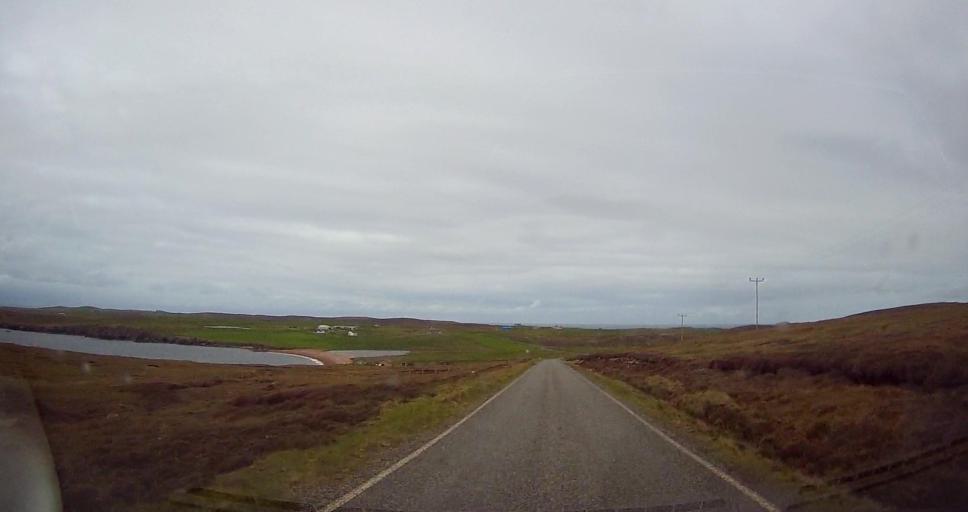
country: GB
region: Scotland
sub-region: Shetland Islands
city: Lerwick
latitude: 60.4879
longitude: -1.5374
